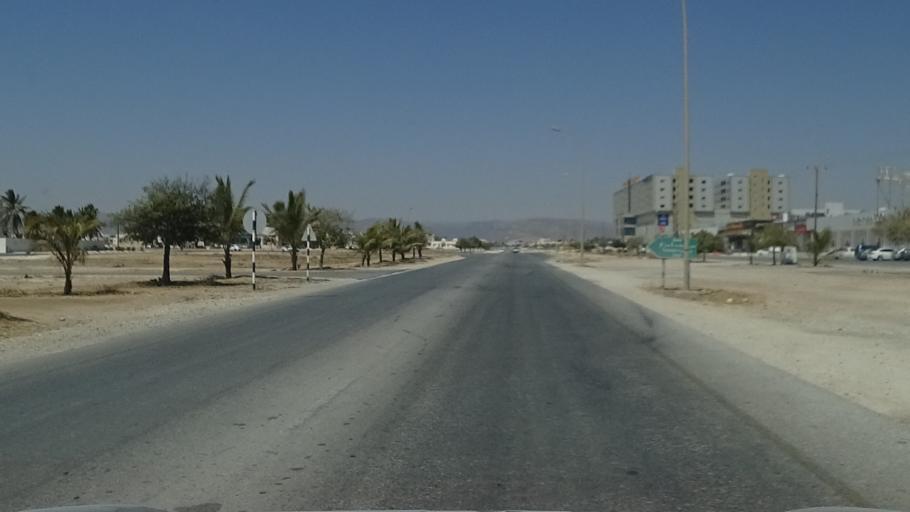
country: OM
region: Zufar
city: Salalah
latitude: 17.0482
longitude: 54.1684
